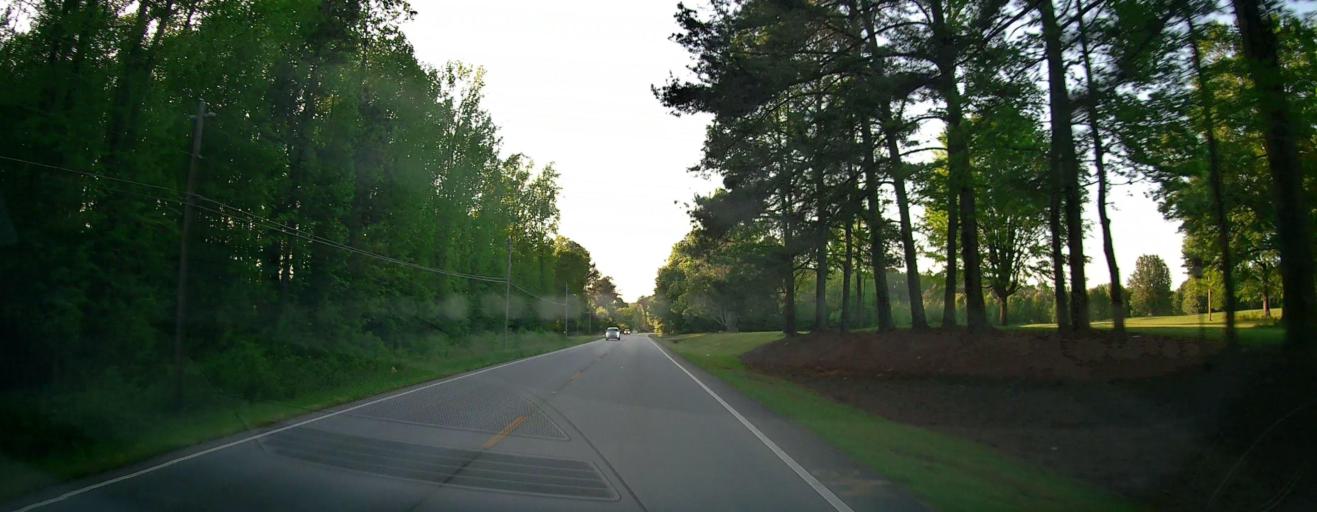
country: US
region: Georgia
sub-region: Newton County
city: Covington
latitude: 33.5777
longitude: -83.7756
